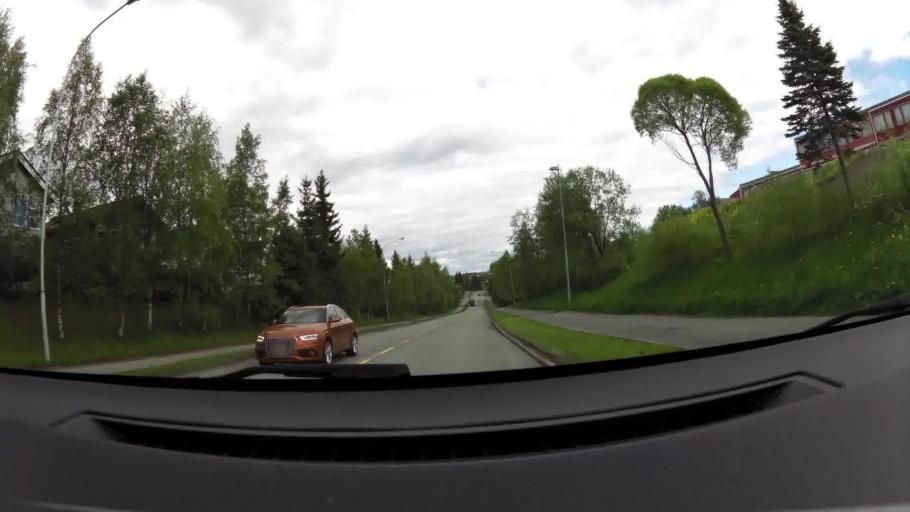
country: NO
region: Sor-Trondelag
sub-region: Trondheim
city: Trondheim
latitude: 63.3976
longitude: 10.4219
